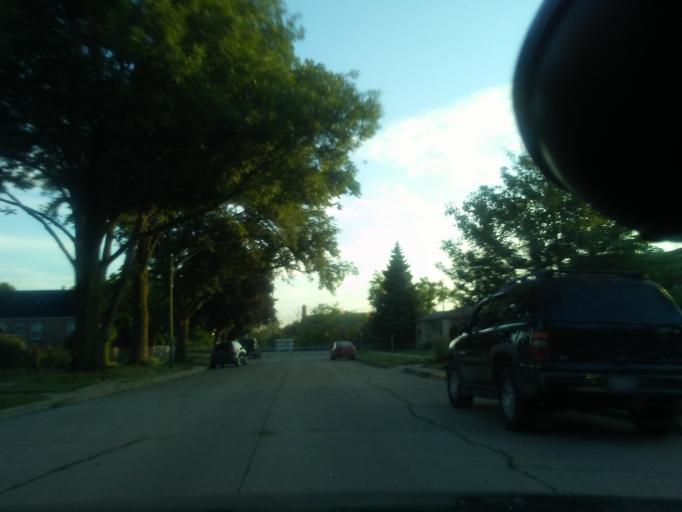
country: US
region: Illinois
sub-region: Cook County
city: Harwood Heights
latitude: 41.9786
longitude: -87.7796
